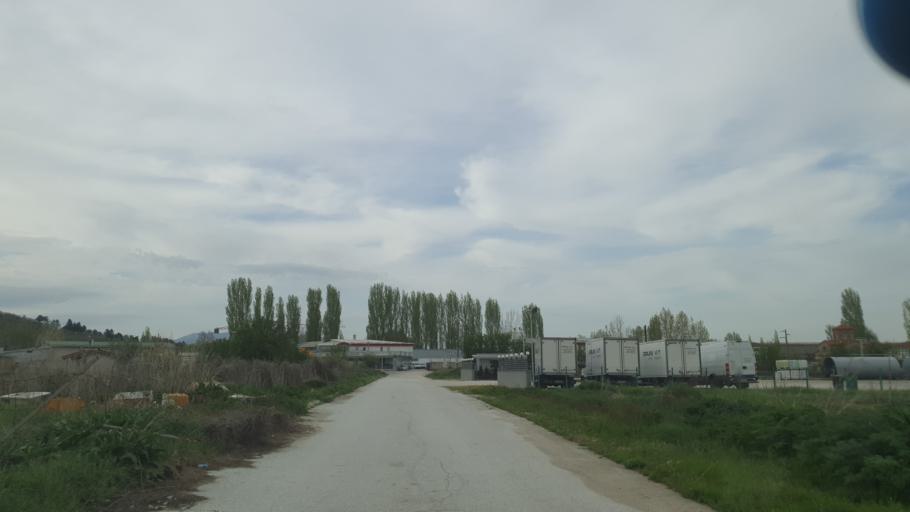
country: MK
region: Bitola
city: Bitola
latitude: 41.0352
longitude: 21.3511
